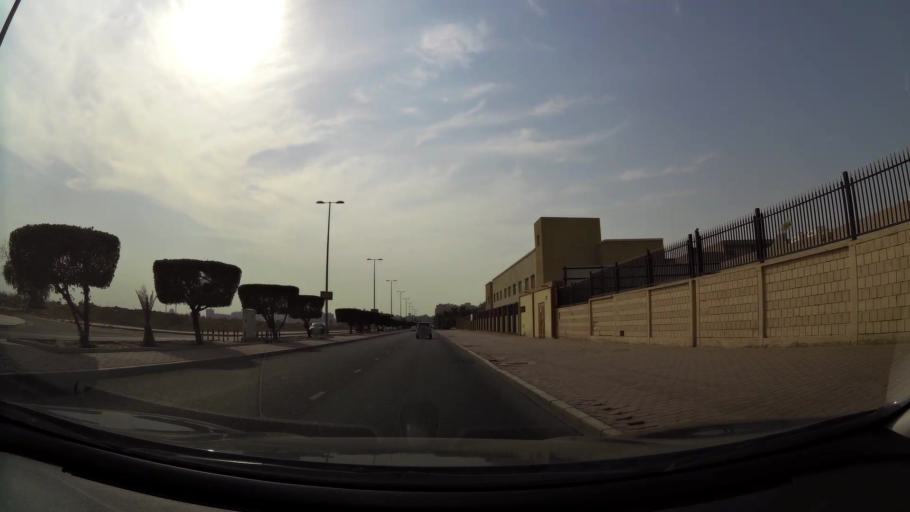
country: KW
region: Al Farwaniyah
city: Janub as Surrah
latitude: 29.2778
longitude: 47.9816
